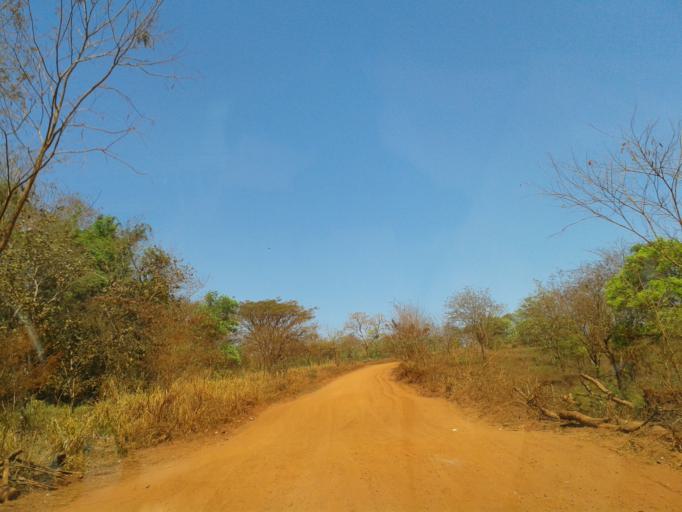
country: BR
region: Minas Gerais
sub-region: Ituiutaba
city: Ituiutaba
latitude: -18.9757
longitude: -49.4201
